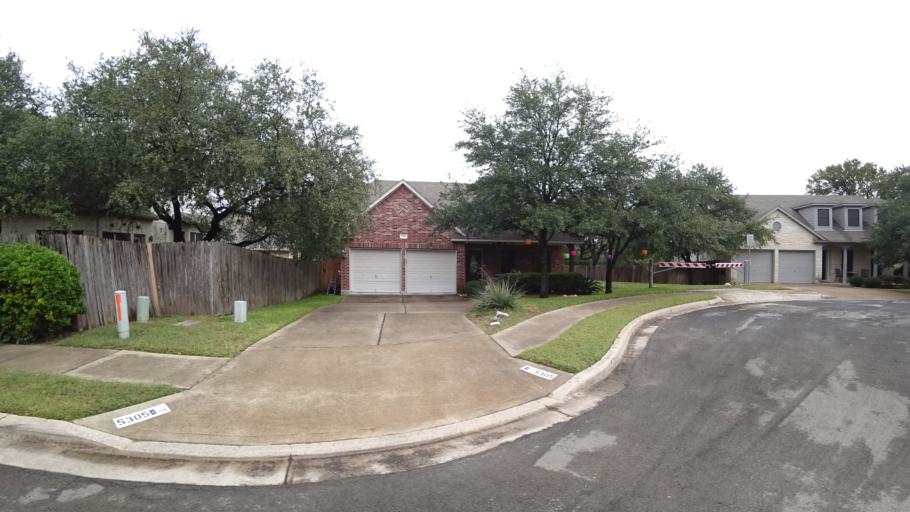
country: US
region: Texas
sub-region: Travis County
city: Shady Hollow
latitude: 30.1935
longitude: -97.8691
